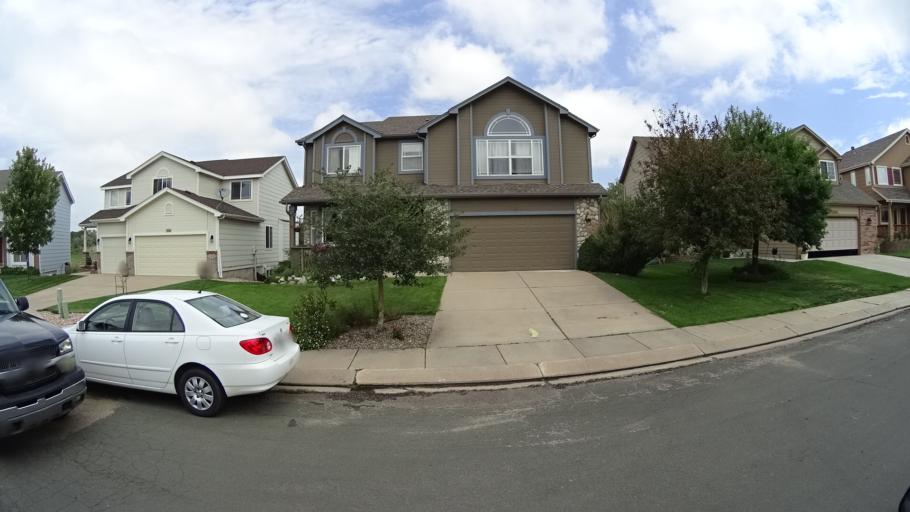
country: US
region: Colorado
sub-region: El Paso County
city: Gleneagle
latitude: 39.0100
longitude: -104.8036
